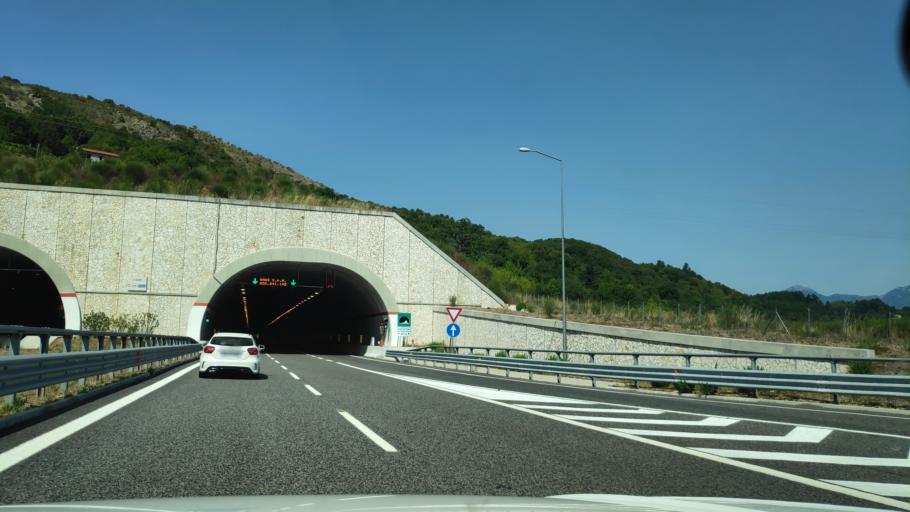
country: IT
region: Calabria
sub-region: Provincia di Cosenza
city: Mormanno
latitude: 39.9004
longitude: 15.9743
